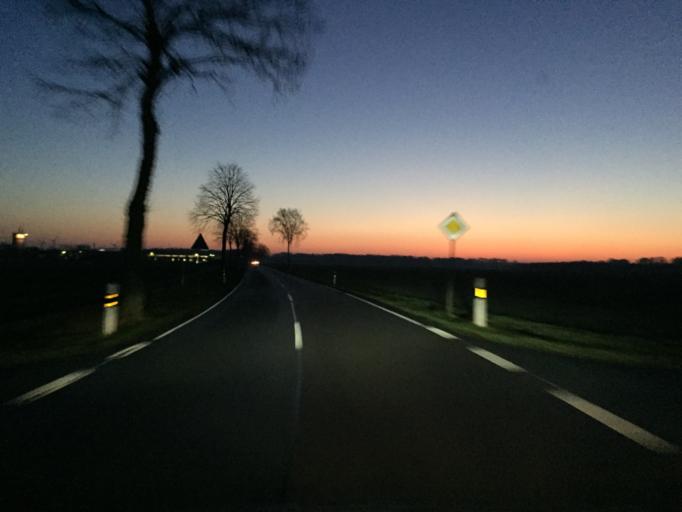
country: DE
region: Lower Saxony
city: Kirchdorf
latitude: 52.6048
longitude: 8.9133
